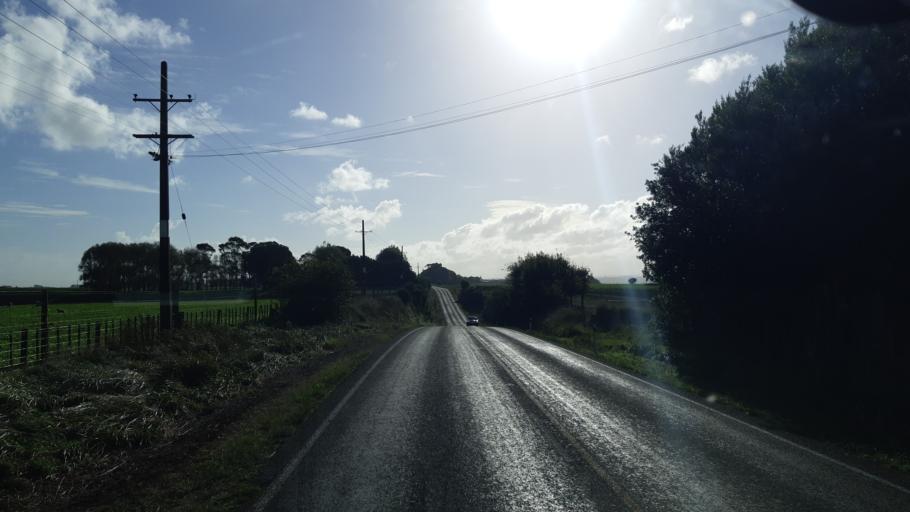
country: NZ
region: Manawatu-Wanganui
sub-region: Wanganui District
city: Wanganui
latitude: -39.9541
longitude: 175.1657
